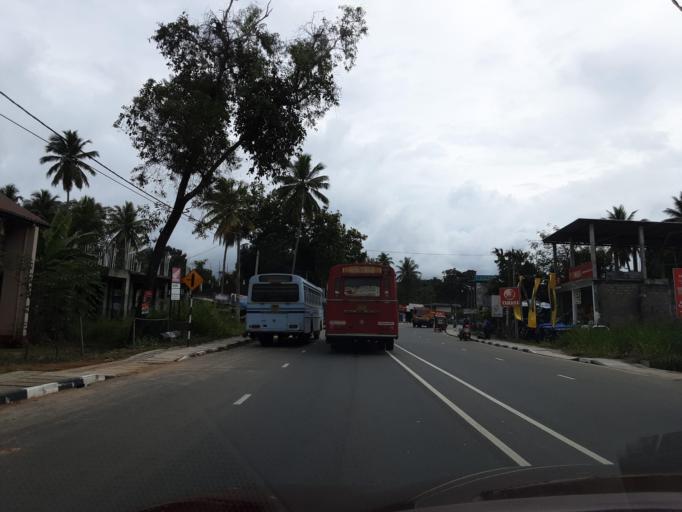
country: LK
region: Eastern Province
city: Ampara
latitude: 7.4011
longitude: 81.2433
